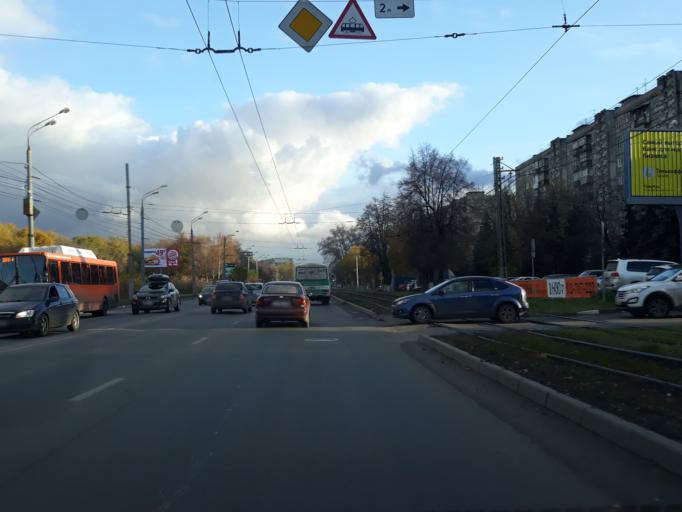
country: RU
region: Nizjnij Novgorod
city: Neklyudovo
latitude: 56.3401
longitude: 43.8802
